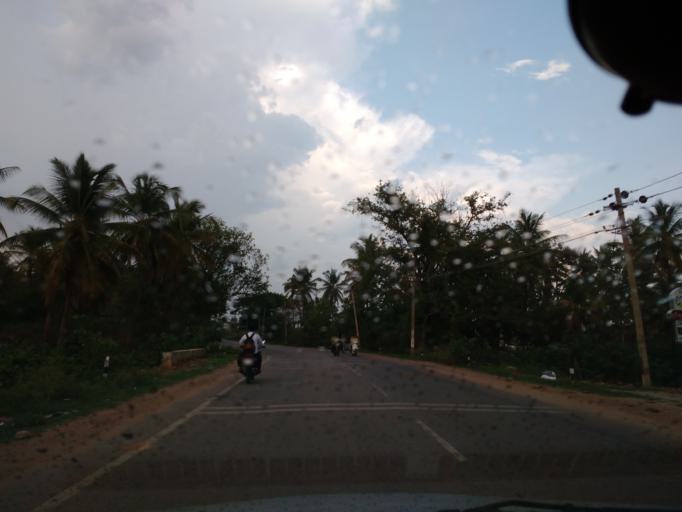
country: IN
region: Karnataka
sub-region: Tumkur
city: Tiptur
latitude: 13.2616
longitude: 76.4895
